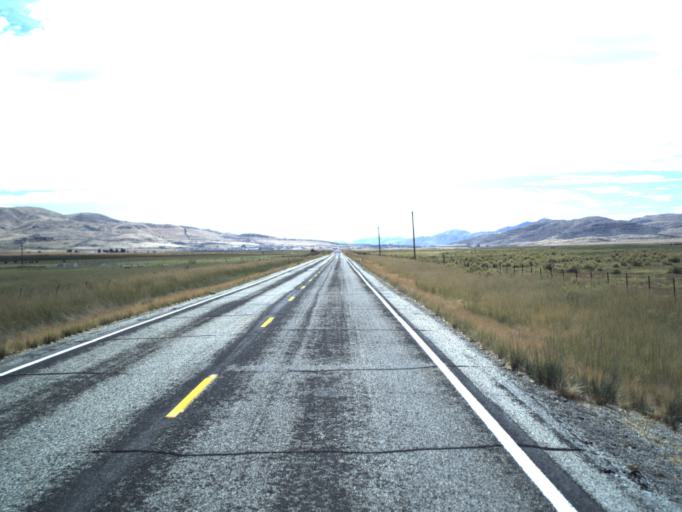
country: US
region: Utah
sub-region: Box Elder County
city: Tremonton
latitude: 41.7607
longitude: -112.4349
